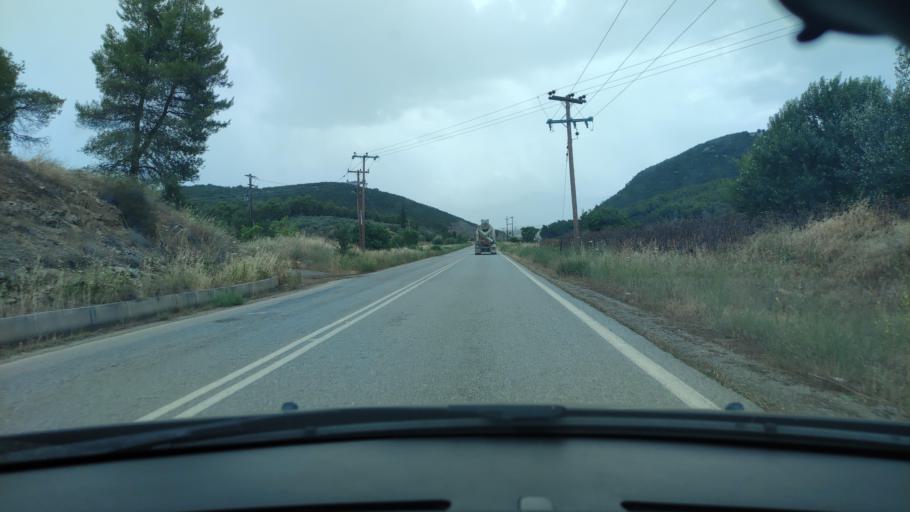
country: GR
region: Central Greece
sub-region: Nomos Evvoias
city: Afration
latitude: 38.5152
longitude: 23.7104
